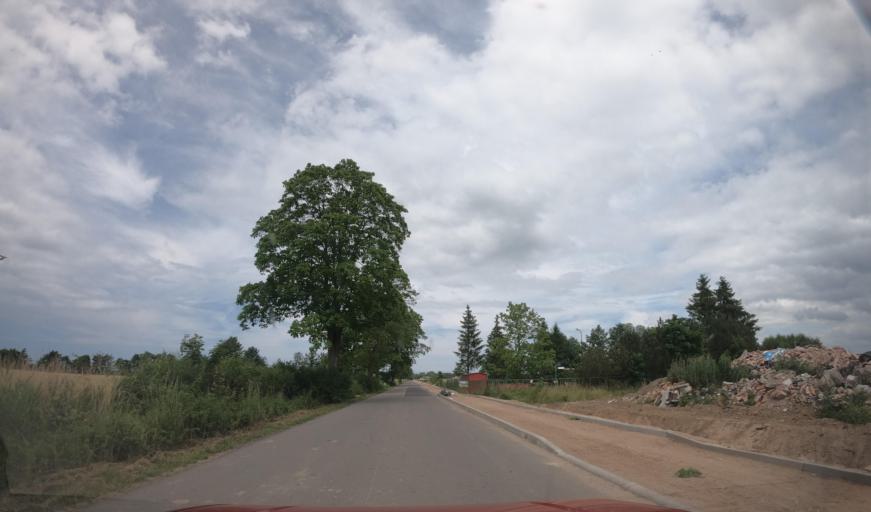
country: PL
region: West Pomeranian Voivodeship
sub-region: Powiat koszalinski
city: Mielno
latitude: 54.2298
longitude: 16.1053
